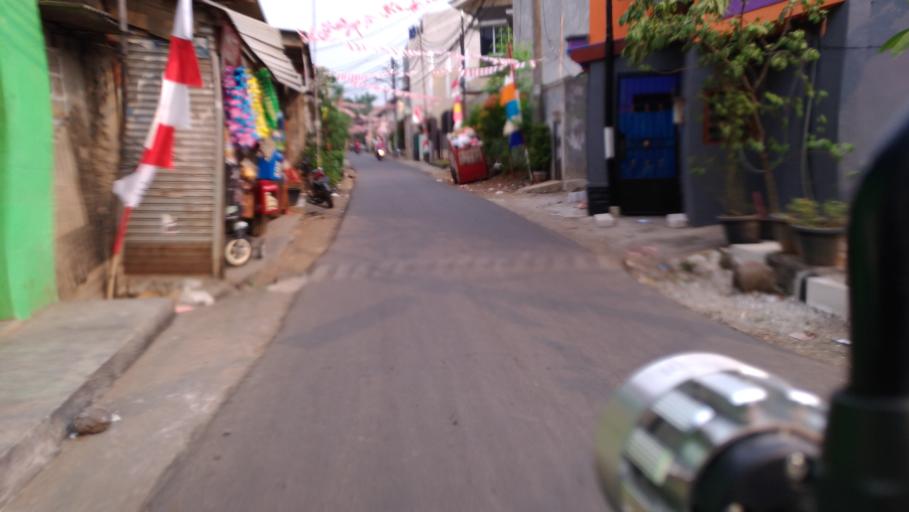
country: ID
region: West Java
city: Depok
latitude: -6.3530
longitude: 106.8826
